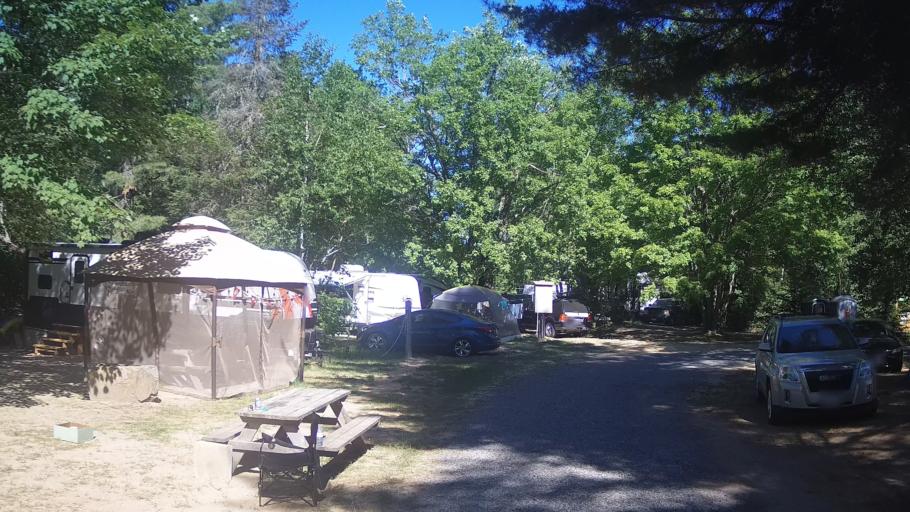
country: CA
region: Ontario
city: Huntsville
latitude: 45.3770
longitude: -79.2158
